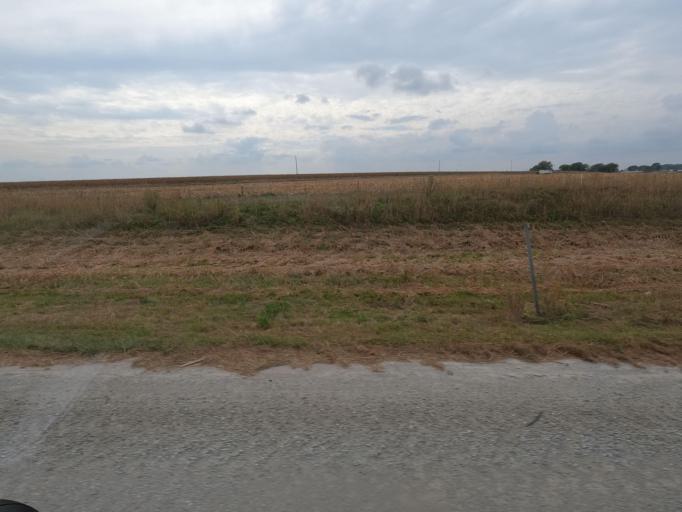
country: US
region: Iowa
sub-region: Jasper County
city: Monroe
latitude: 41.5093
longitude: -93.0861
